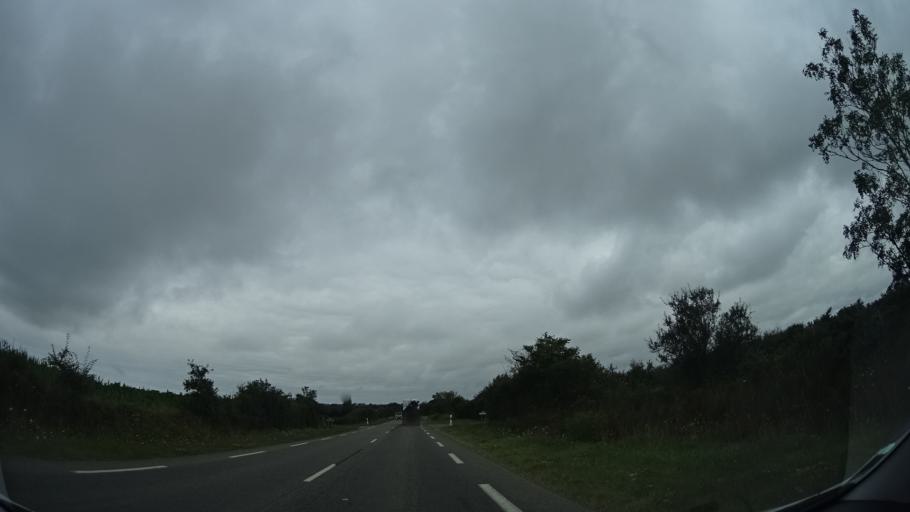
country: FR
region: Lower Normandy
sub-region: Departement de la Manche
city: Portbail
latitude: 49.3558
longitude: -1.6814
